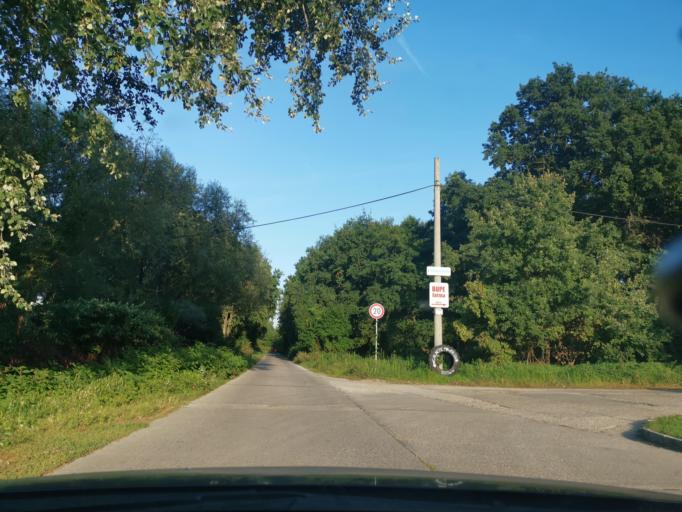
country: SK
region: Trnavsky
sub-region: Okres Senica
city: Senica
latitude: 48.6598
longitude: 17.2690
